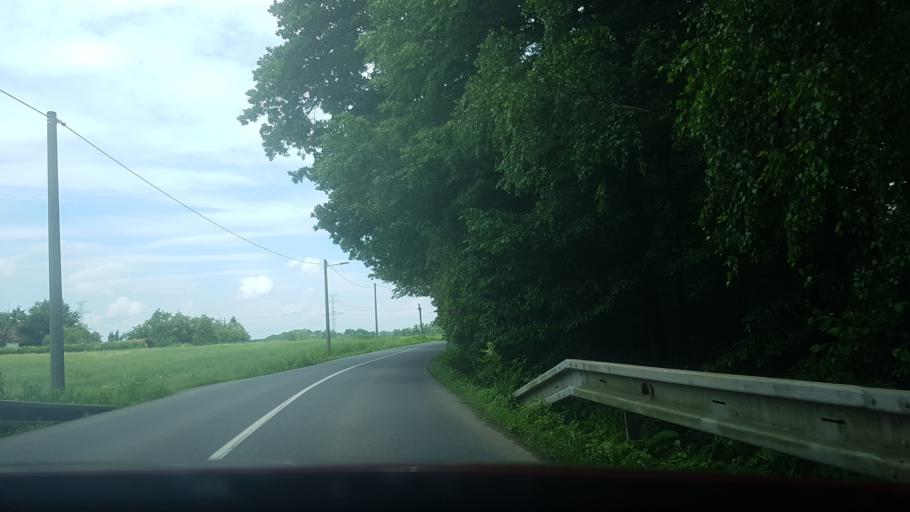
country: CZ
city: Dobra
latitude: 49.6891
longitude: 18.4286
